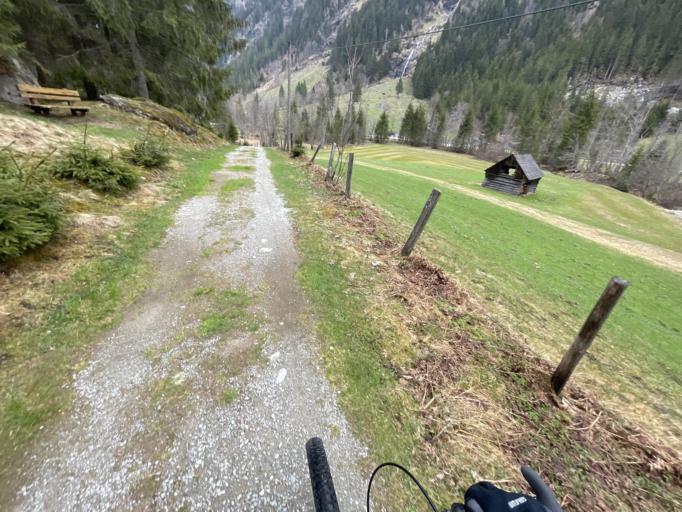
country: AT
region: Styria
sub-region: Politischer Bezirk Liezen
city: Haus
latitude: 47.3343
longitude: 13.7448
